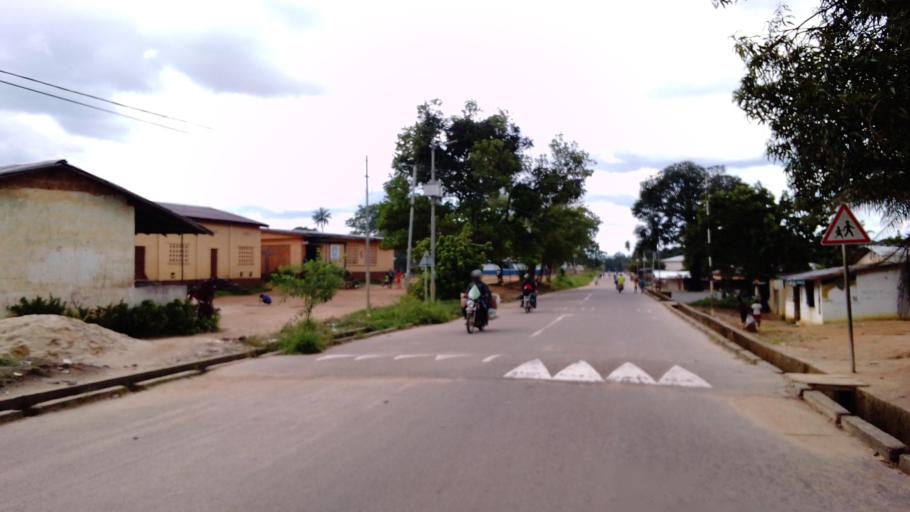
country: SL
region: Eastern Province
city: Koidu
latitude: 8.6537
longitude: -10.9754
